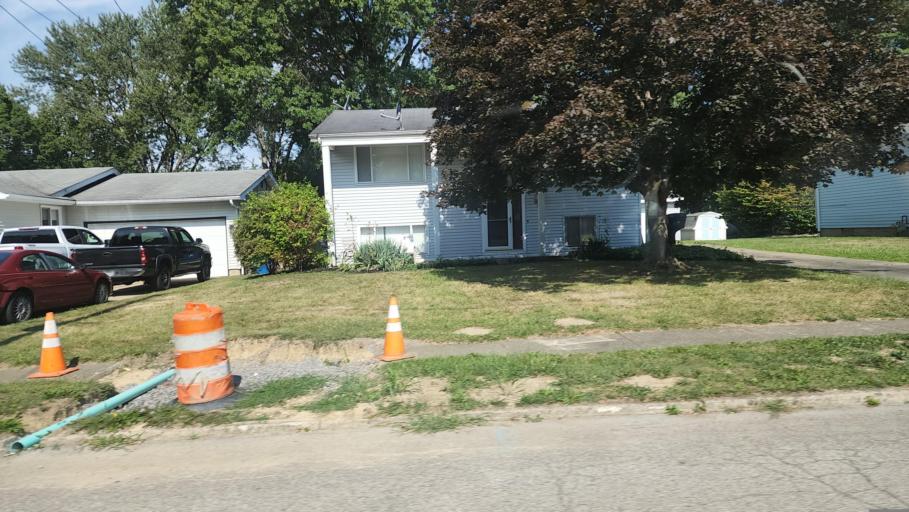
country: US
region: Ohio
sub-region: Trumbull County
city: Niles
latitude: 41.1924
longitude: -80.7556
